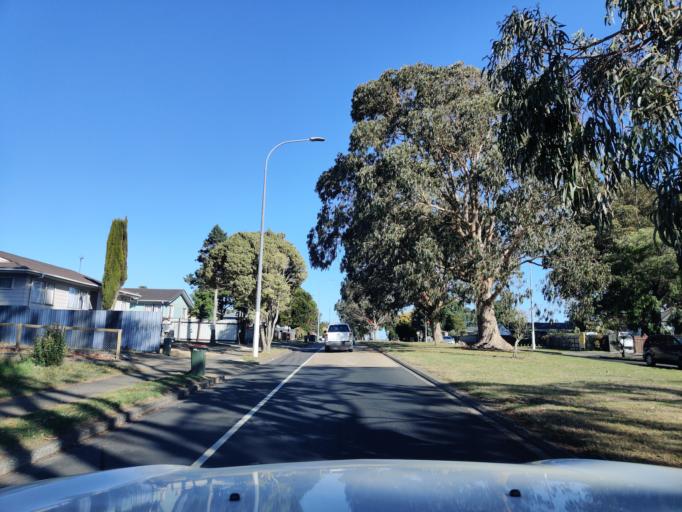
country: NZ
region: Auckland
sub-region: Auckland
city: Wiri
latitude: -37.0246
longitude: 174.8654
